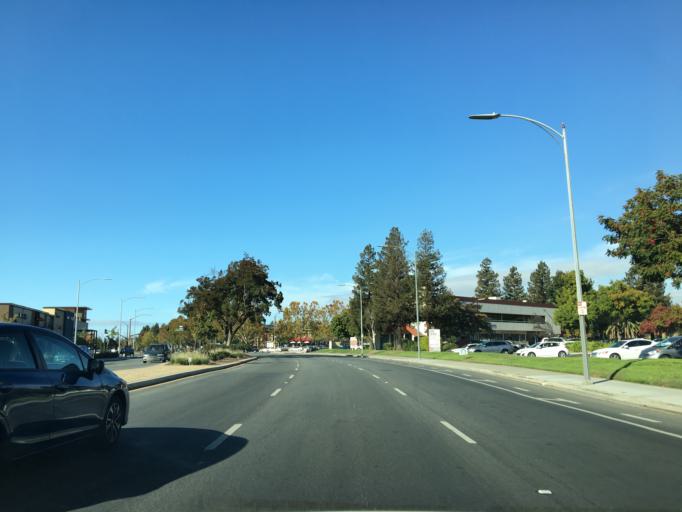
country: US
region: California
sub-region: Santa Clara County
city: San Jose
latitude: 37.3812
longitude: -121.8953
